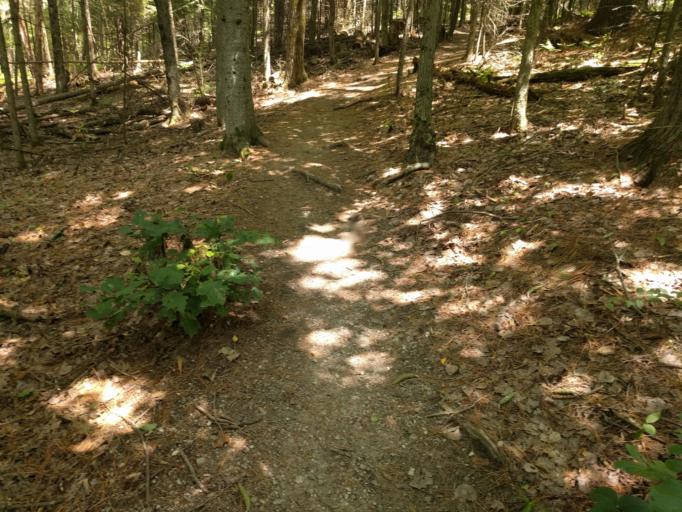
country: CA
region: Quebec
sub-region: Outaouais
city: Wakefield
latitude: 45.6341
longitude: -75.9354
